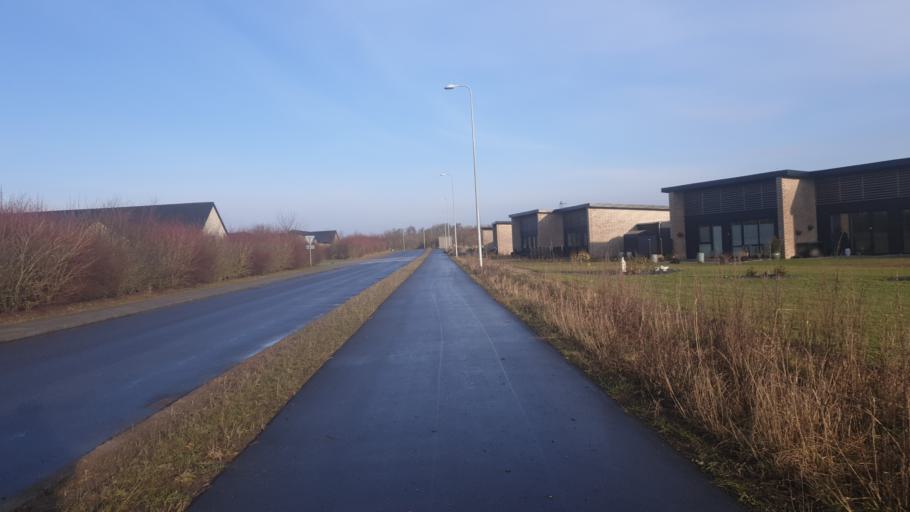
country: DK
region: Central Jutland
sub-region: Hedensted Kommune
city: Hedensted
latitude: 55.7642
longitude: 9.7238
